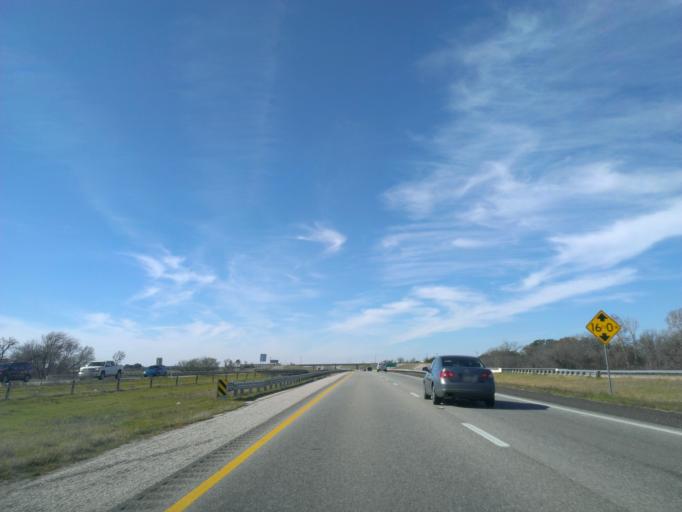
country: US
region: Texas
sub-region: Bell County
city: Nolanville
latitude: 31.0664
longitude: -97.5774
